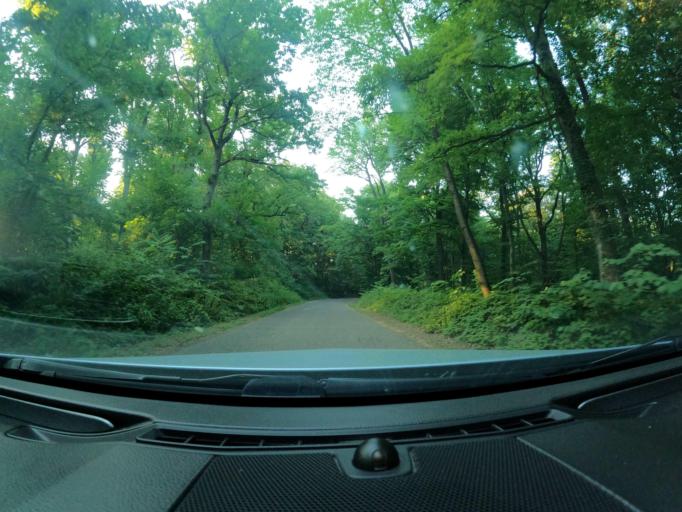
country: RS
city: Vrdnik
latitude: 45.1600
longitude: 19.7568
